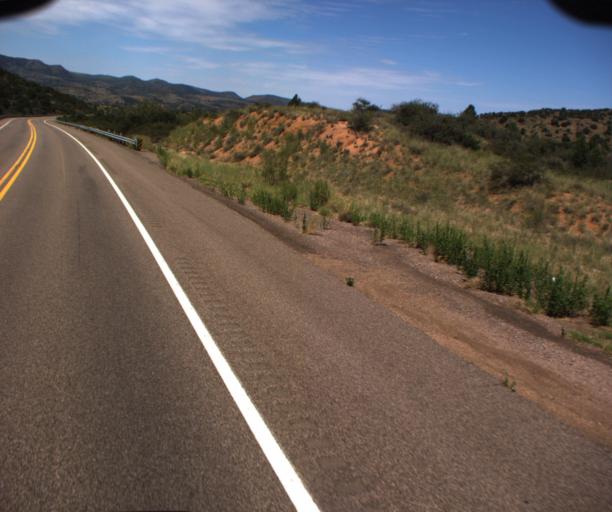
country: US
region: Arizona
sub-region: Gila County
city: Globe
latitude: 33.6123
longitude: -110.6153
